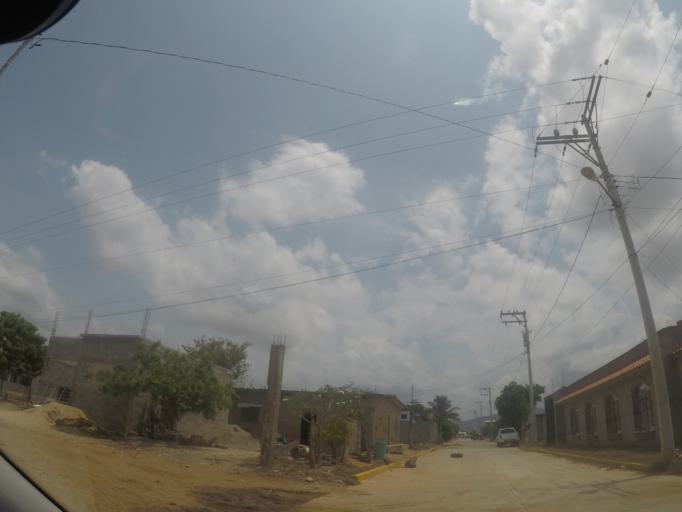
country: MX
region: Oaxaca
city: El Espinal
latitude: 16.5564
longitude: -94.9445
